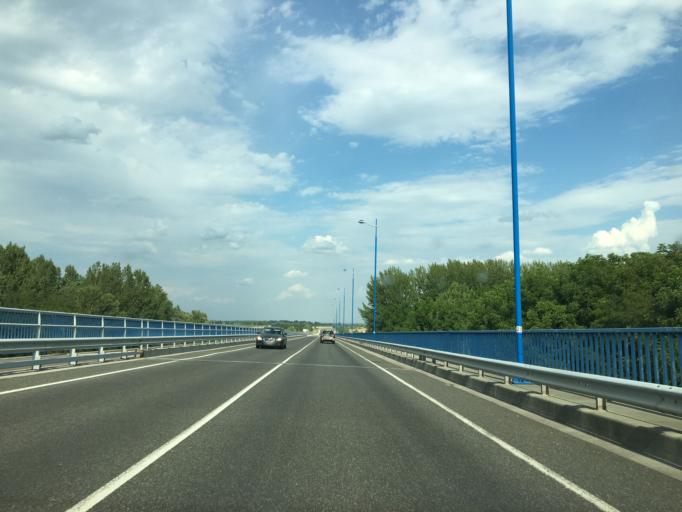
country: HU
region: Bacs-Kiskun
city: Dusnok
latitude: 46.3523
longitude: 18.8983
